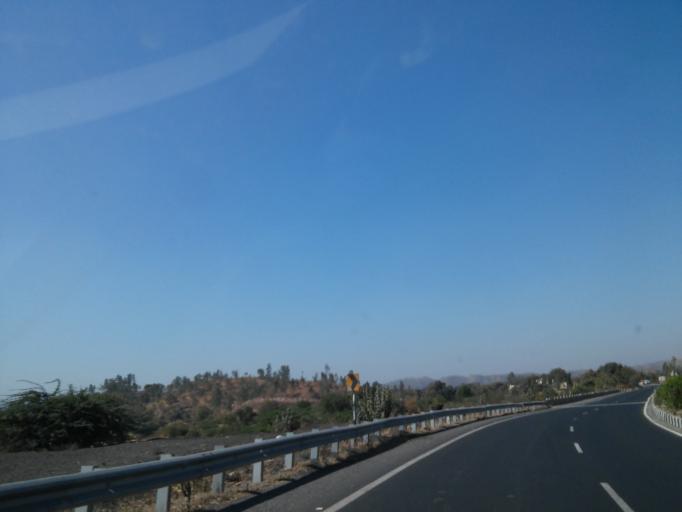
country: IN
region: Gujarat
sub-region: Sabar Kantha
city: Meghraj
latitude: 23.7403
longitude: 73.4316
